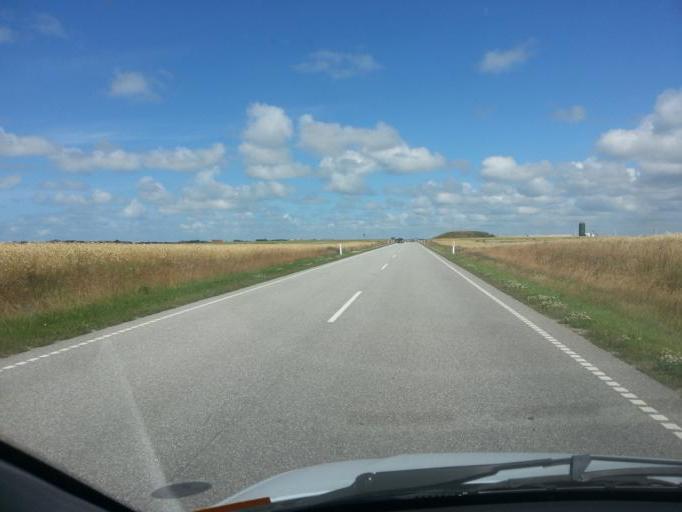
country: DK
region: Central Jutland
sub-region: Lemvig Kommune
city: Harboore
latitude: 56.4753
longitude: 8.1438
